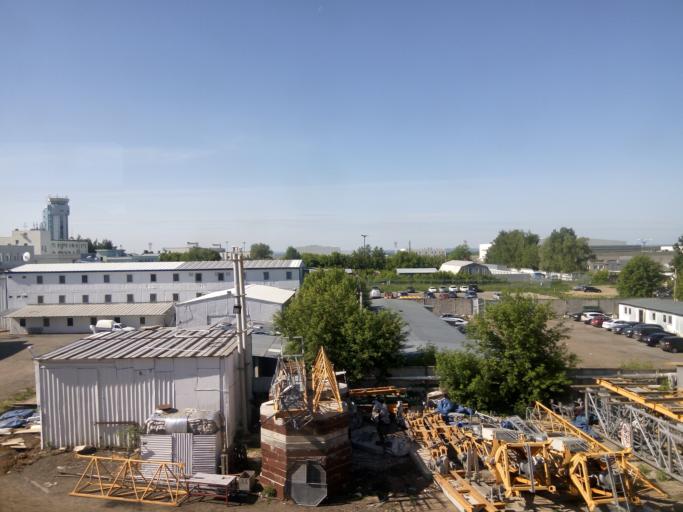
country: RU
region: Tatarstan
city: Stolbishchi
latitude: 55.6153
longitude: 49.2839
